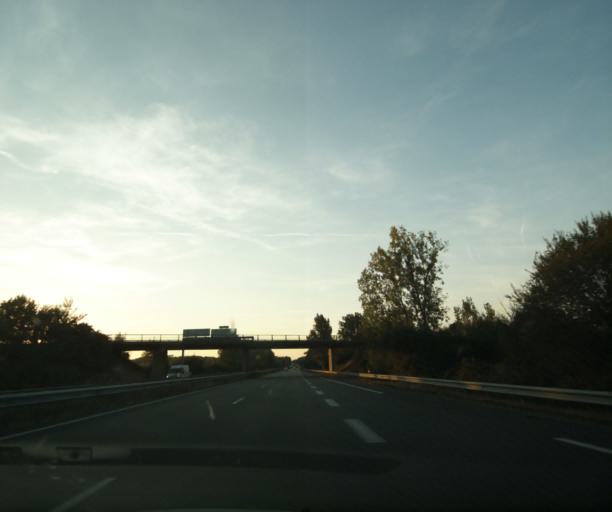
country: FR
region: Aquitaine
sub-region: Departement du Lot-et-Garonne
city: Fourques-sur-Garonne
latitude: 44.4328
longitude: 0.1300
